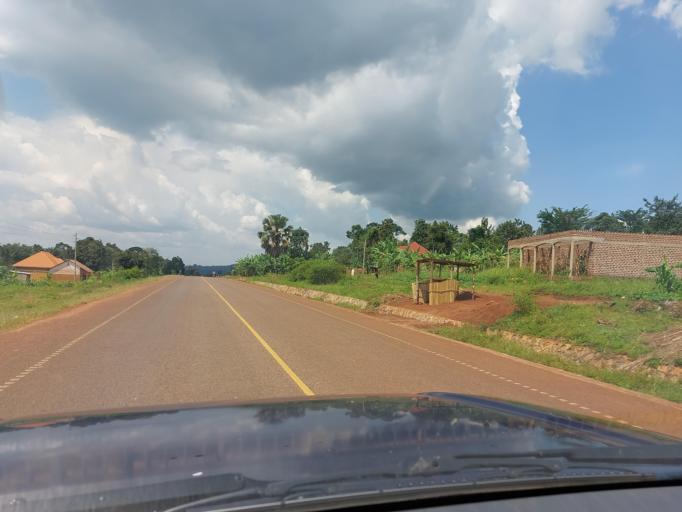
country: UG
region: Central Region
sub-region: Buikwe District
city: Njeru
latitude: 0.3306
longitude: 33.1181
